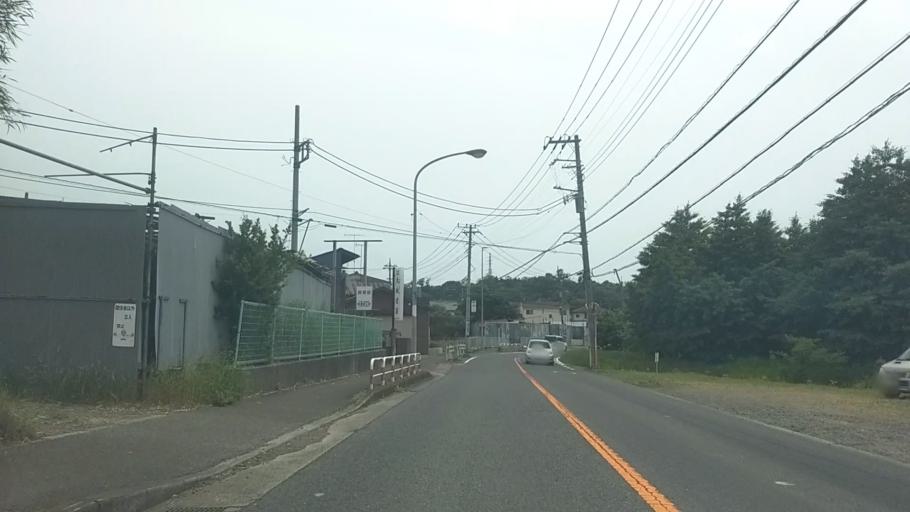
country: JP
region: Kanagawa
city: Chigasaki
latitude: 35.3631
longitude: 139.4219
